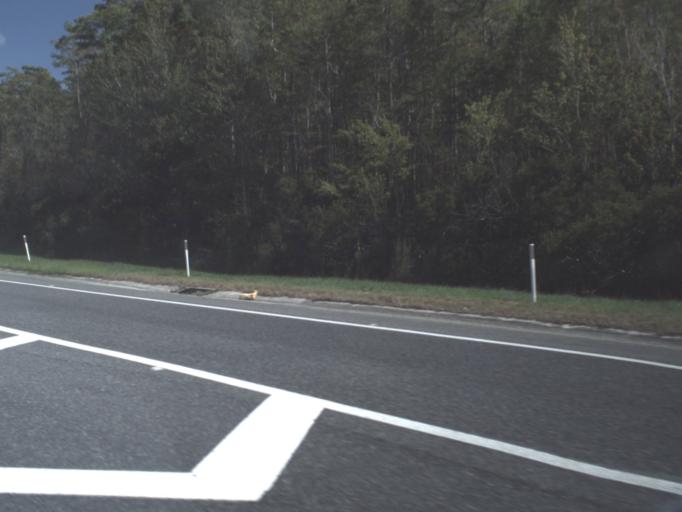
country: US
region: Florida
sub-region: Osceola County
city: Celebration
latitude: 28.3464
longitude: -81.5116
